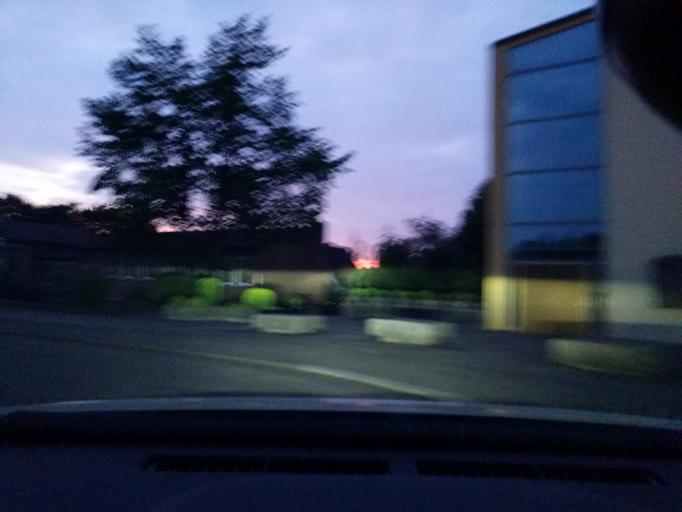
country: DE
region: Rheinland-Pfalz
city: Kaiserslautern
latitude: 49.4460
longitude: 7.7430
